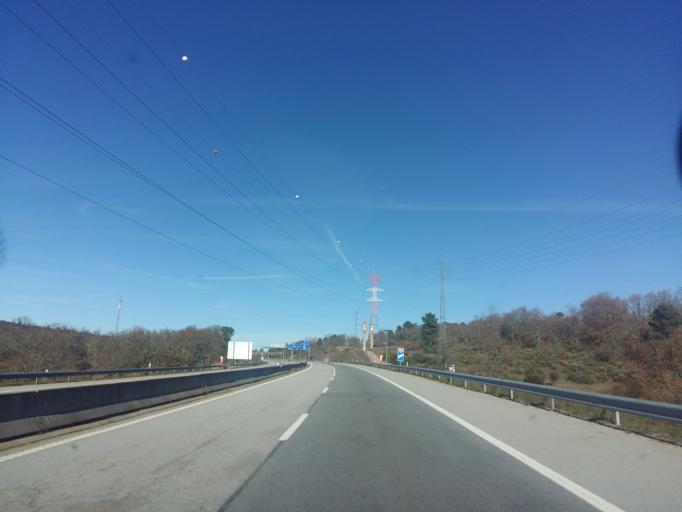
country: PT
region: Guarda
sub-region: Guarda
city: Sequeira
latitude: 40.5555
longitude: -7.2168
